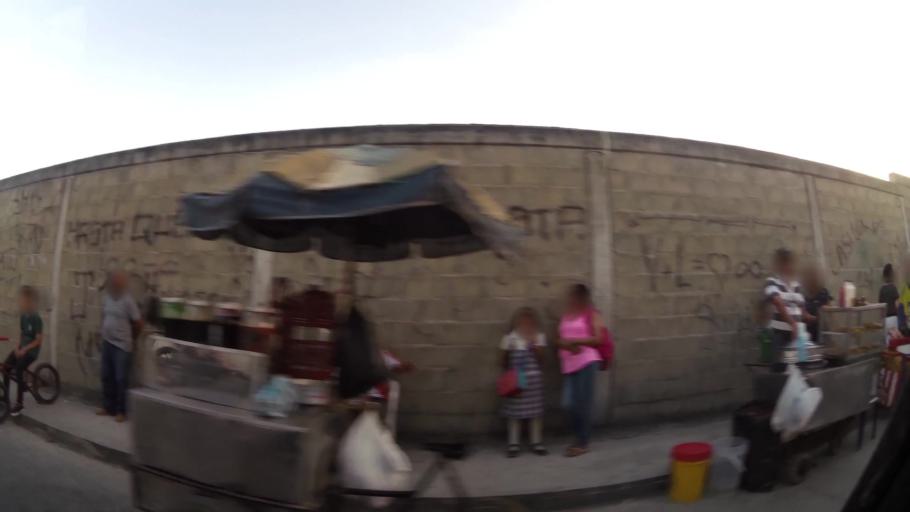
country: CO
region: Atlantico
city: Soledad
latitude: 10.9301
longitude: -74.7790
